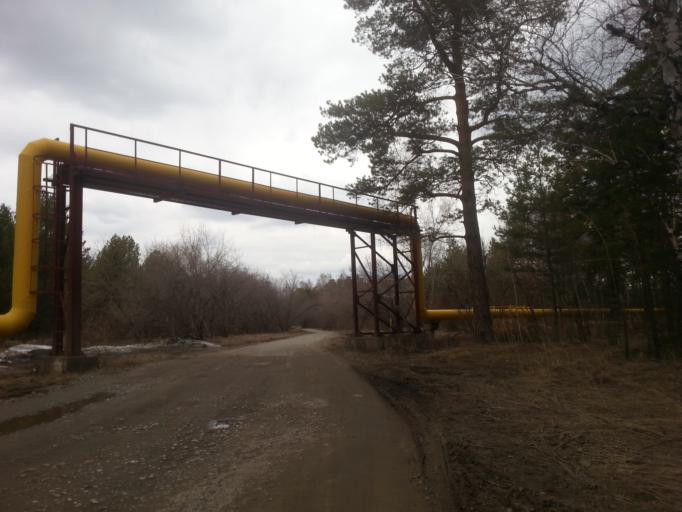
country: RU
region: Altai Krai
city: Yuzhnyy
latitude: 53.2855
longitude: 83.7309
